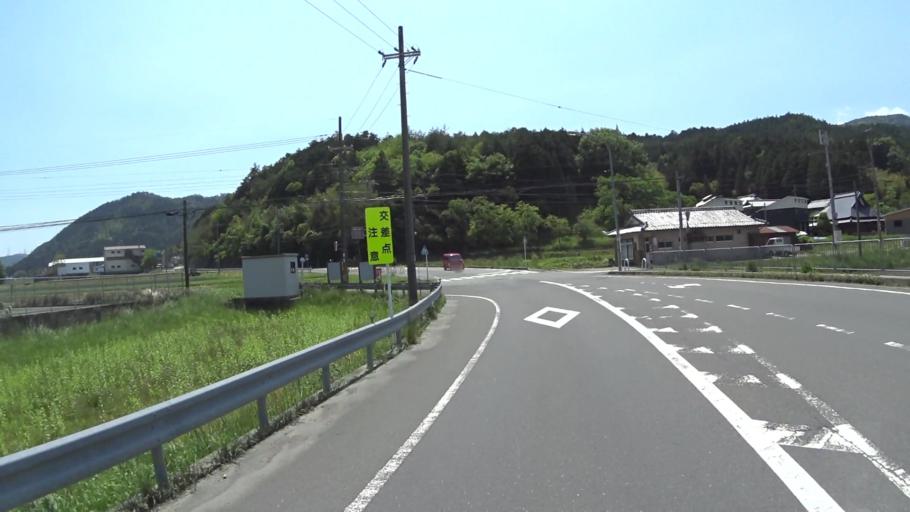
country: JP
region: Kyoto
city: Kameoka
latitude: 35.0361
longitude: 135.4851
